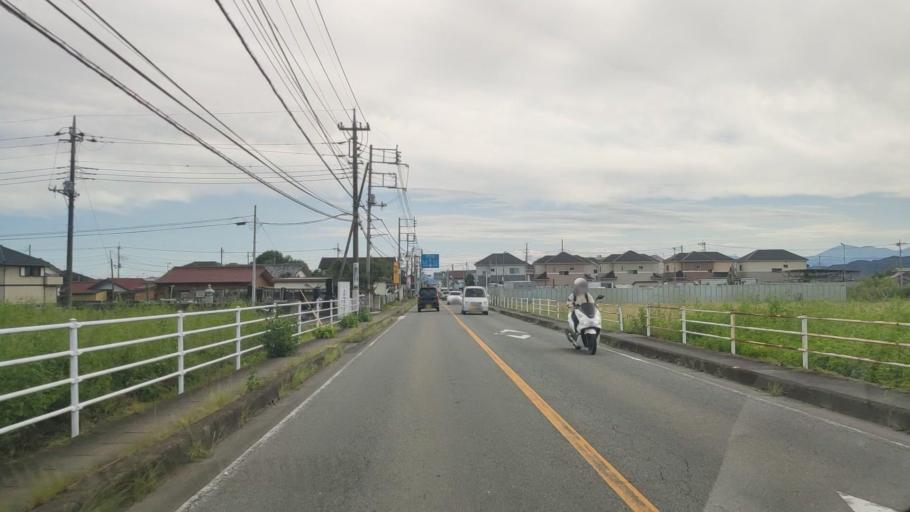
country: JP
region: Gunma
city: Kanekomachi
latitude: 36.3670
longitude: 138.9756
